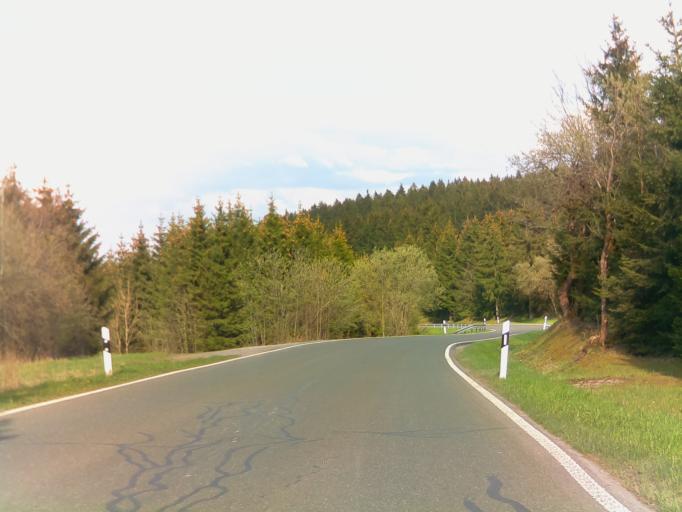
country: DE
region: Bavaria
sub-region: Upper Franconia
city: Tettau
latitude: 50.4915
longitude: 11.2685
